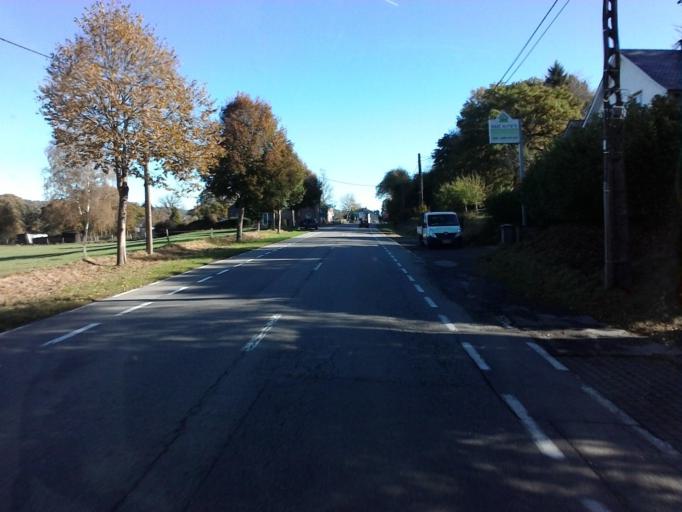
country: BE
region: Wallonia
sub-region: Province de Liege
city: Stavelot
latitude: 50.4080
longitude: 5.9658
